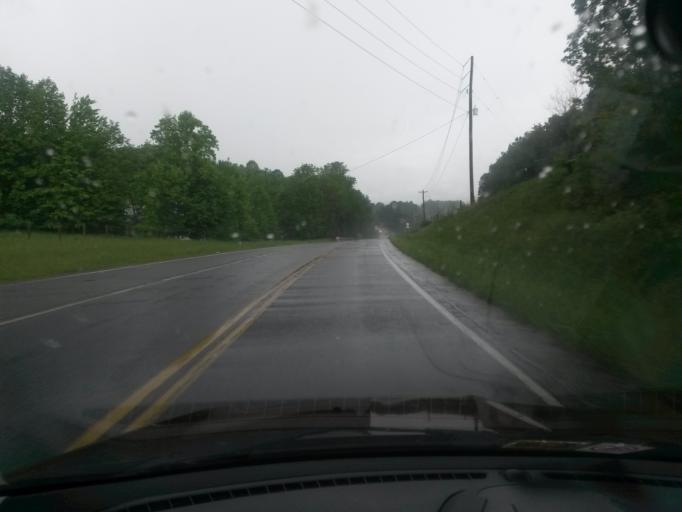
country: US
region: Virginia
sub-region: Floyd County
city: Floyd
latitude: 36.9746
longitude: -80.3994
